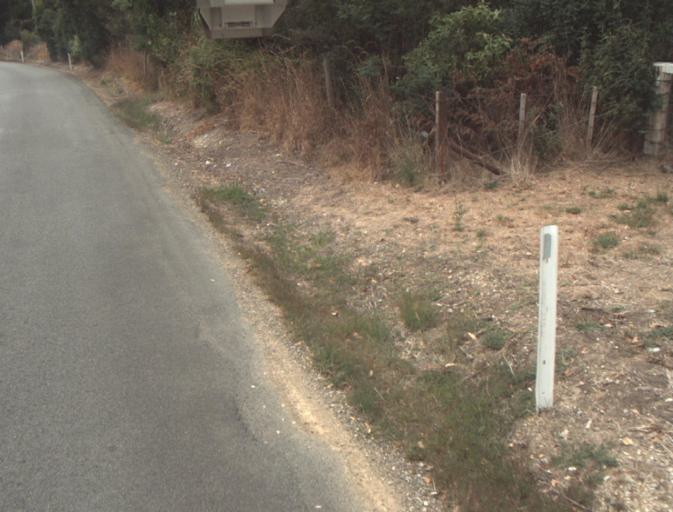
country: AU
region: Tasmania
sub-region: Launceston
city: Mayfield
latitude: -41.2034
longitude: 147.2172
